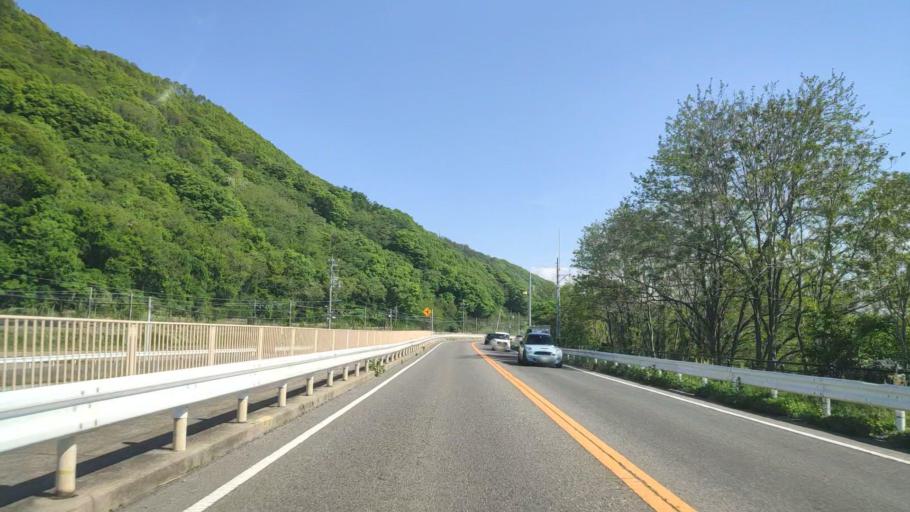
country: JP
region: Nagano
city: Matsumoto
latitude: 36.2626
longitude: 137.9471
